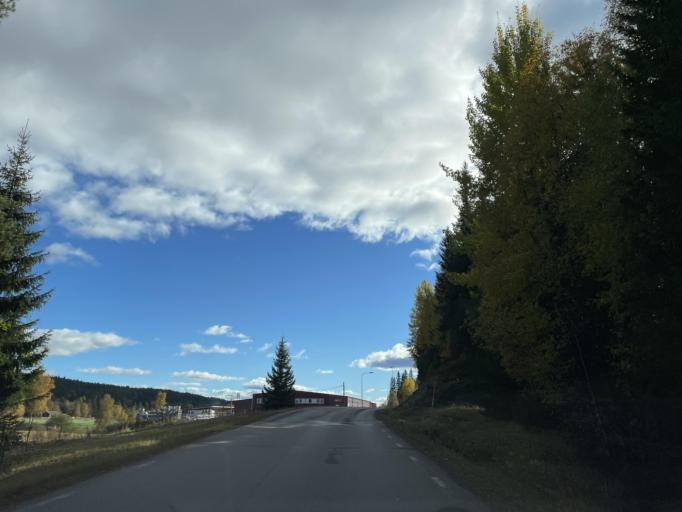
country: SE
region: Dalarna
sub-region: Malung-Saelens kommun
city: Malung
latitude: 61.1325
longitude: 13.2758
